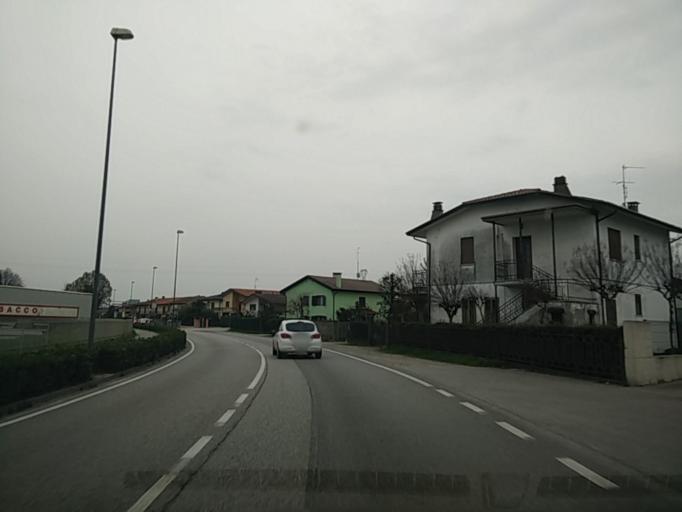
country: IT
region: Veneto
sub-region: Provincia di Venezia
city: Scorze
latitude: 45.5660
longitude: 12.1176
